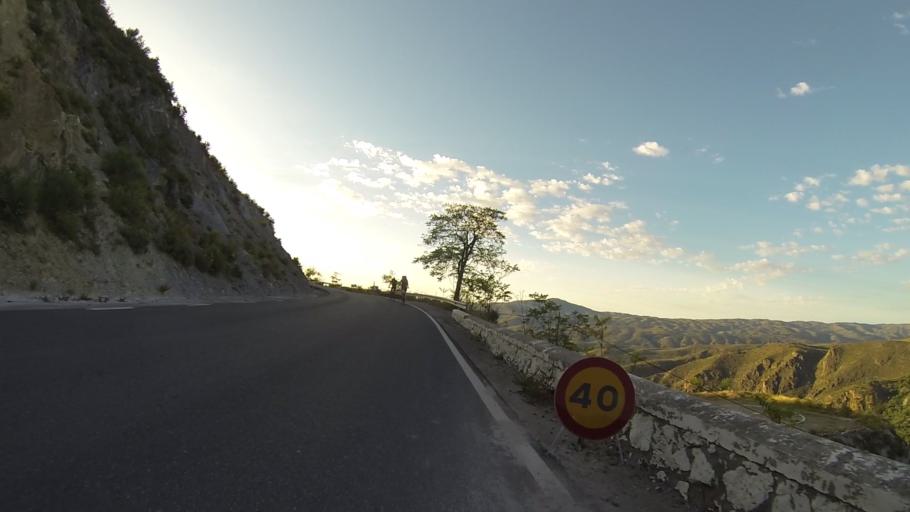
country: ES
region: Andalusia
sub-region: Provincia de Granada
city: Berchules
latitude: 36.9790
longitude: -3.1419
